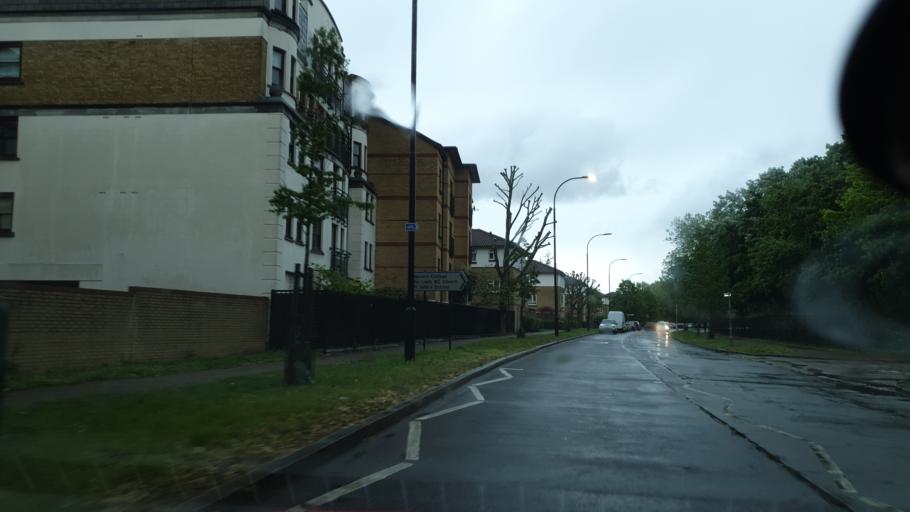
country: GB
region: England
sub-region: Greater London
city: Bethnal Green
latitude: 51.5046
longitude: -0.0455
